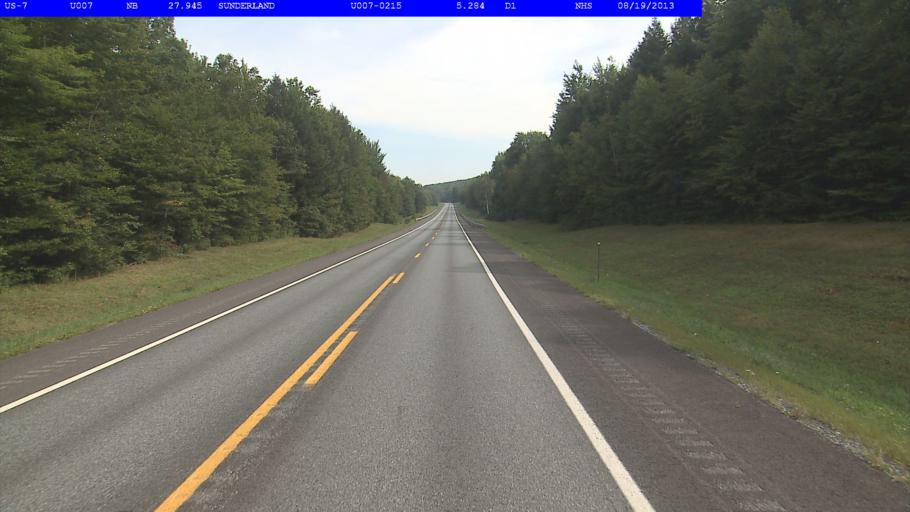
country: US
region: Vermont
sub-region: Bennington County
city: Arlington
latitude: 43.0947
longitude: -73.0988
